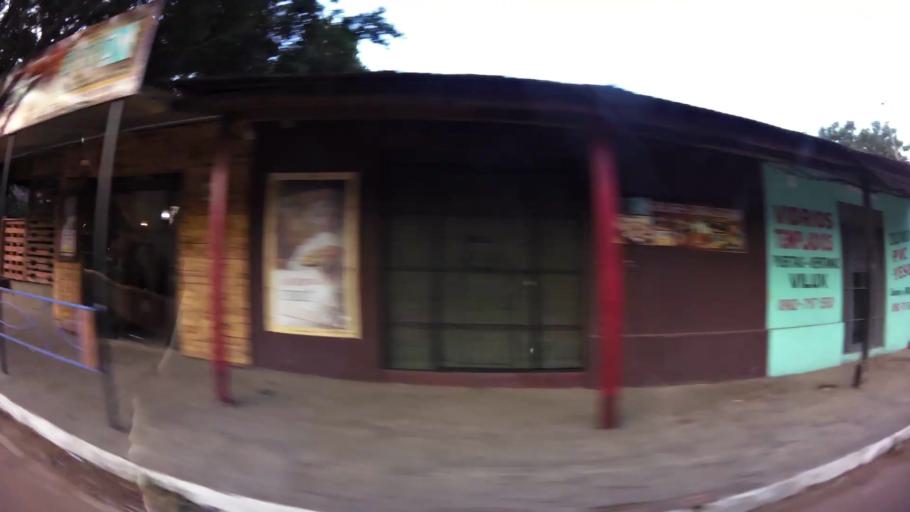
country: PY
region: Central
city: Villa Elisa
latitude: -25.3574
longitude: -57.5963
